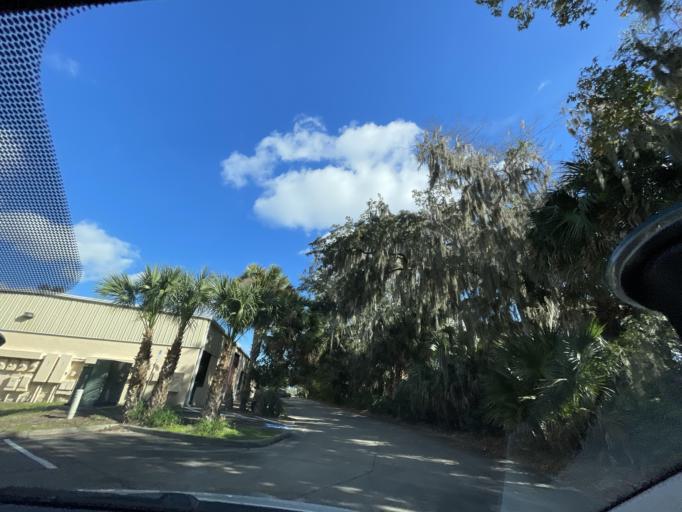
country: US
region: Florida
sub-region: Volusia County
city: South Daytona
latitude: 29.1578
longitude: -81.0235
